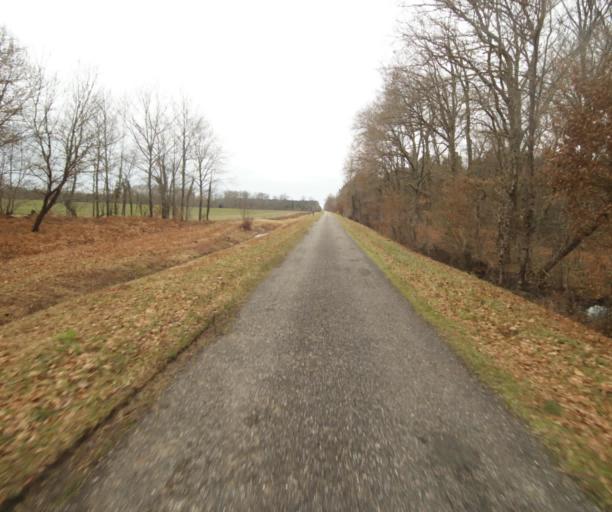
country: FR
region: Aquitaine
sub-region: Departement des Landes
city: Gabarret
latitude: 44.0158
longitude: -0.0364
